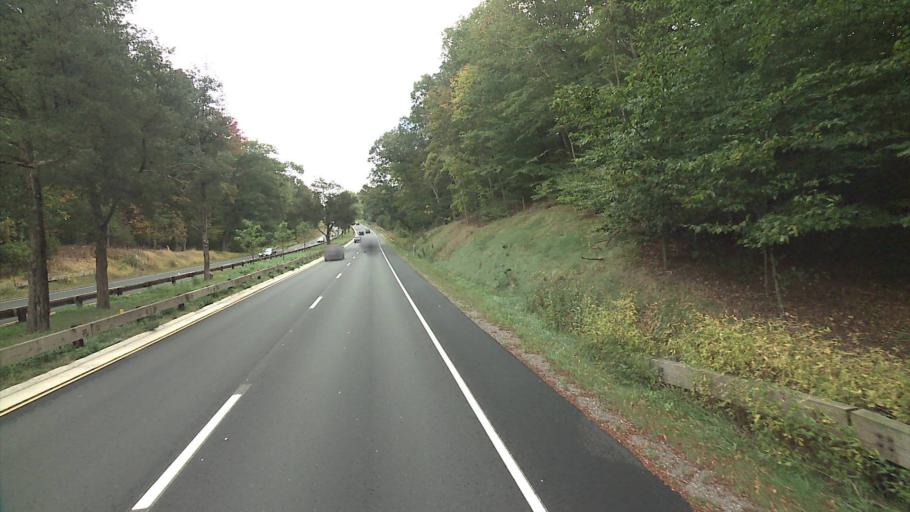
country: US
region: Connecticut
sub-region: Fairfield County
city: North Stamford
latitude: 41.1005
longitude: -73.5882
